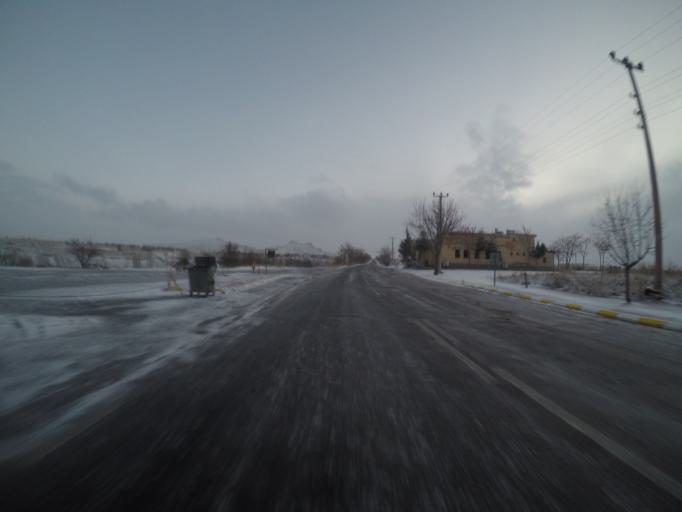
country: TR
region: Nevsehir
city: Goereme
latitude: 38.6199
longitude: 34.8046
